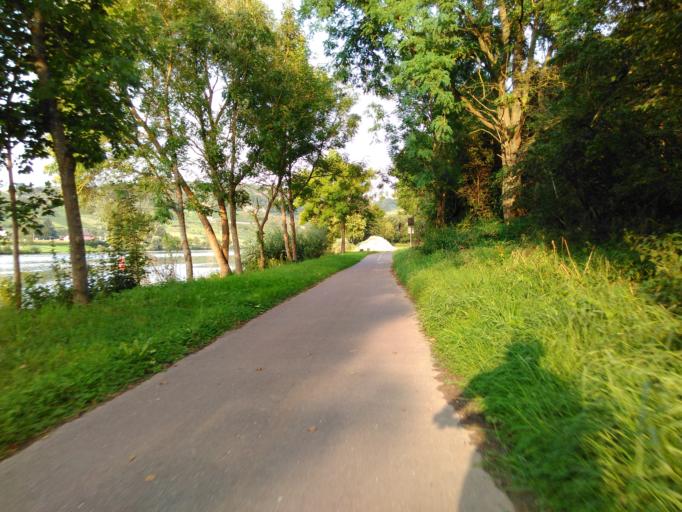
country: LU
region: Grevenmacher
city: Wasserbillig
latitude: 49.7118
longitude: 6.5200
